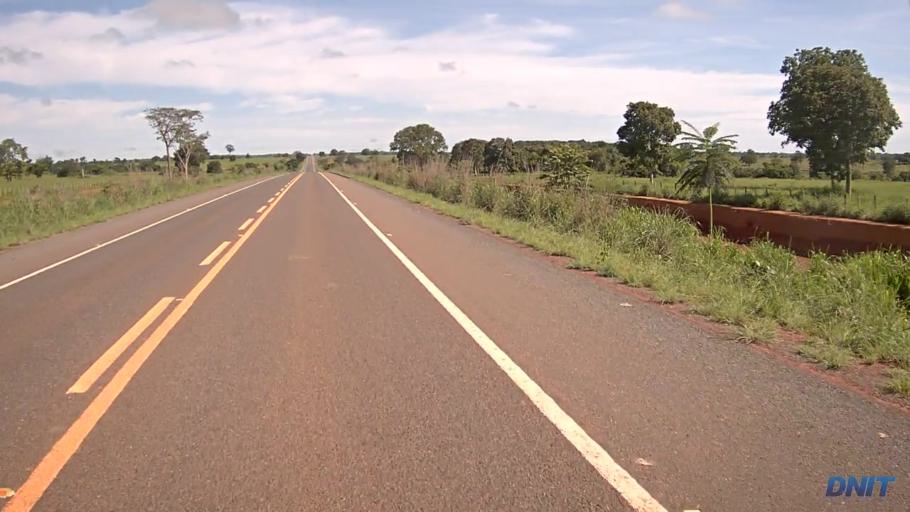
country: BR
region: Goias
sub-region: Sao Miguel Do Araguaia
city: Sao Miguel do Araguaia
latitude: -13.3848
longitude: -50.1396
